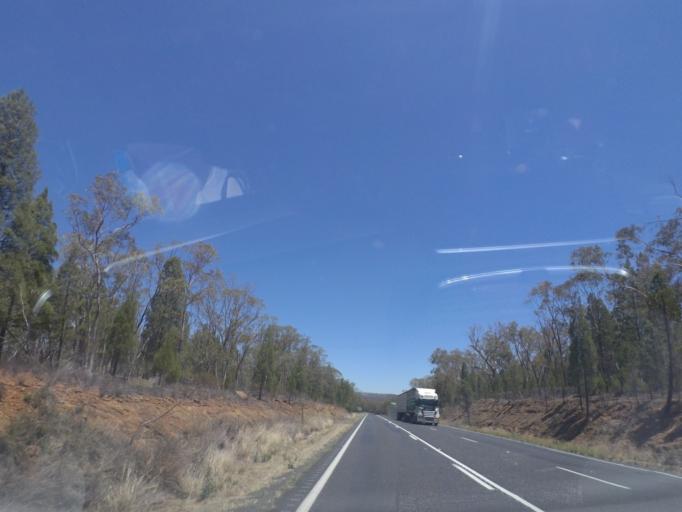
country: AU
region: New South Wales
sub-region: Warrumbungle Shire
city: Coonabarabran
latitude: -31.2354
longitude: 149.3165
